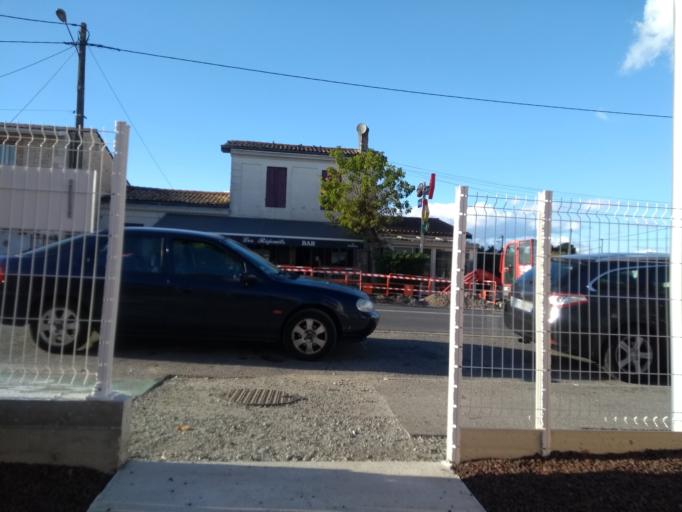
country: FR
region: Aquitaine
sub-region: Departement de la Gironde
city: Cestas
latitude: 44.7378
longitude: -0.6570
